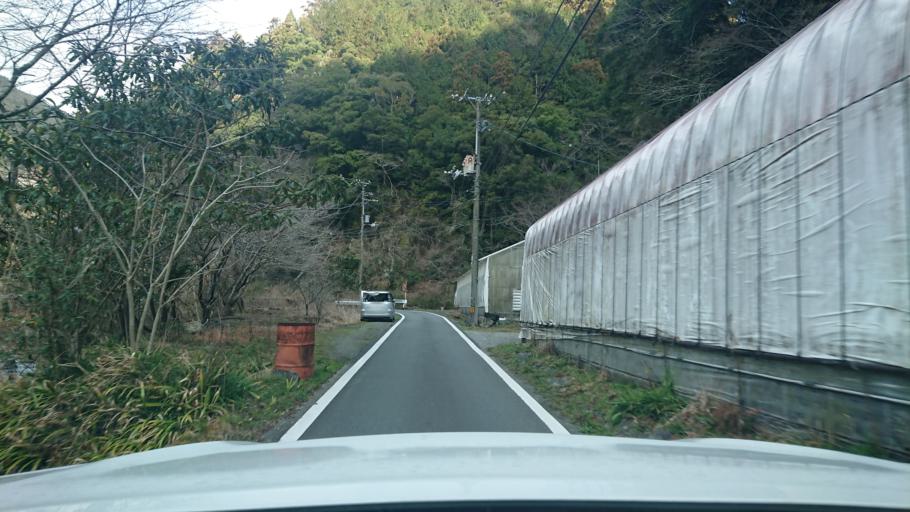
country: JP
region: Tokushima
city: Ishii
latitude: 33.8946
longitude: 134.4033
